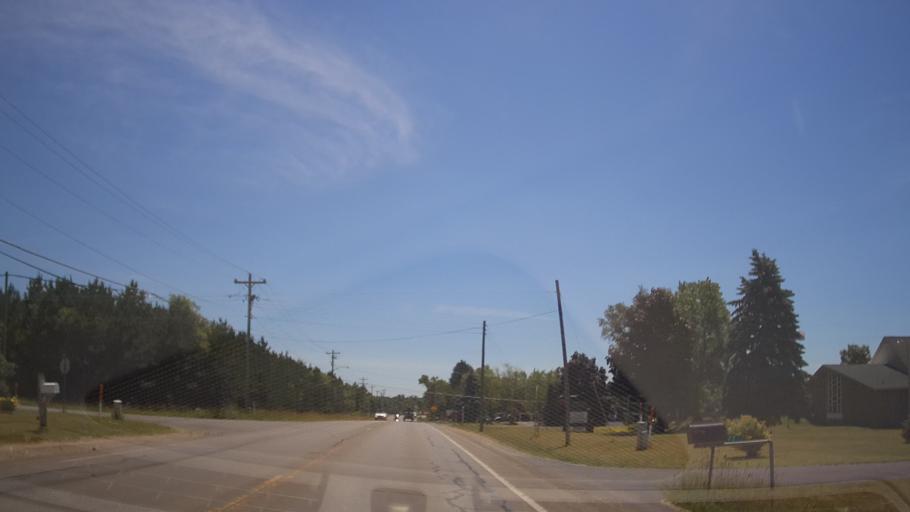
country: US
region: Michigan
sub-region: Grand Traverse County
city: Traverse City
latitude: 44.6690
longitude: -85.6901
